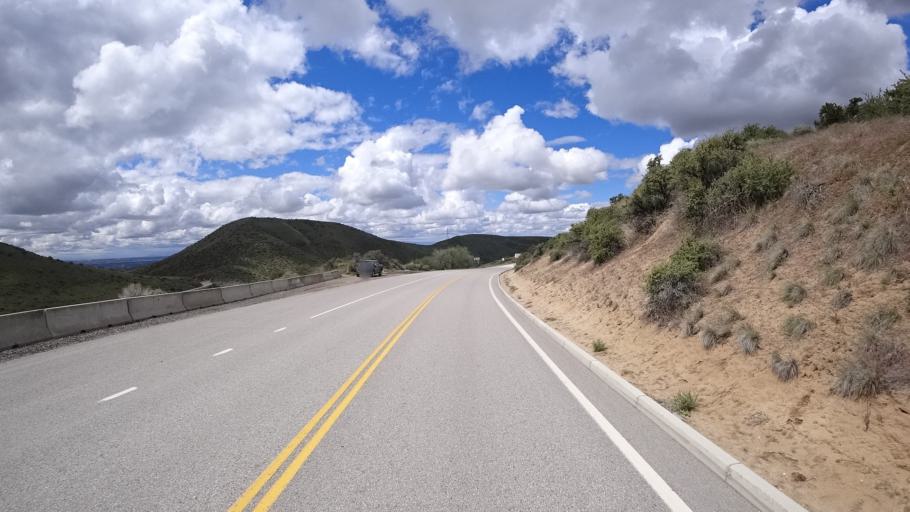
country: US
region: Idaho
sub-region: Ada County
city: Boise
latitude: 43.6899
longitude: -116.1820
